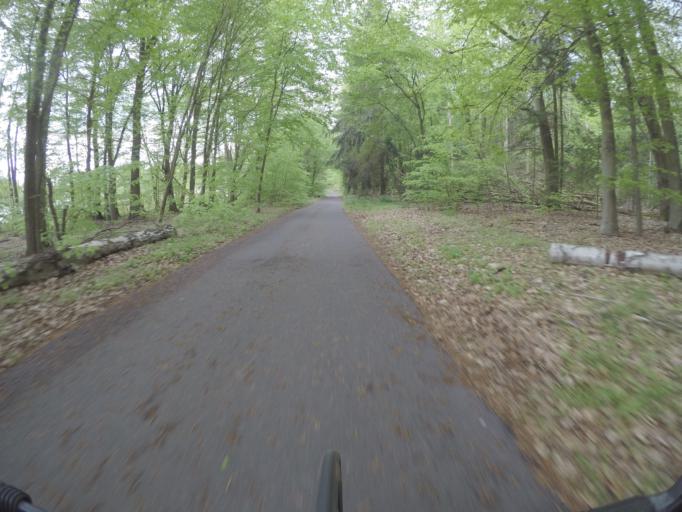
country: DE
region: Brandenburg
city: Marienwerder
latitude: 52.8578
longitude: 13.6124
